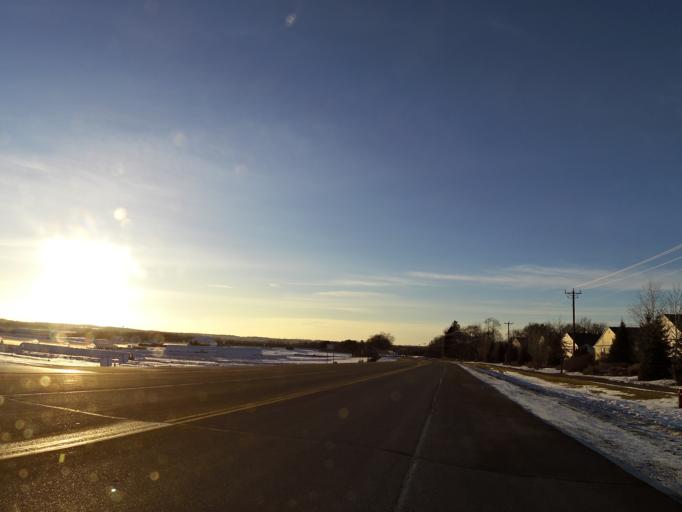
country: US
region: Minnesota
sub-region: Washington County
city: Woodbury
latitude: 44.8908
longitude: -92.8832
